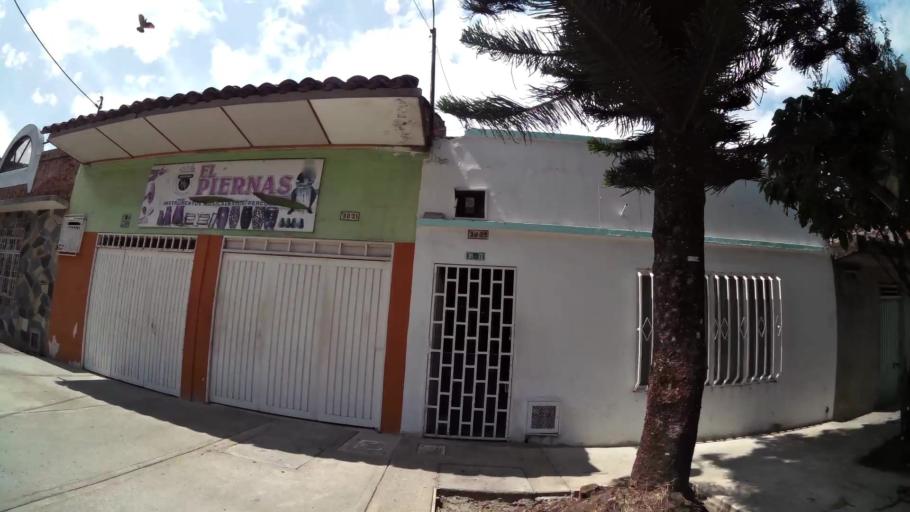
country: CO
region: Valle del Cauca
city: Cali
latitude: 3.4415
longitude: -76.5147
